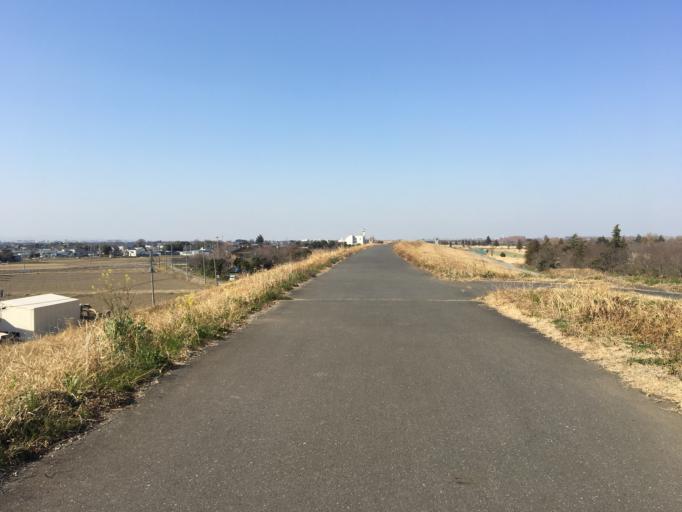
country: JP
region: Saitama
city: Shiki
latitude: 35.8647
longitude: 139.5771
